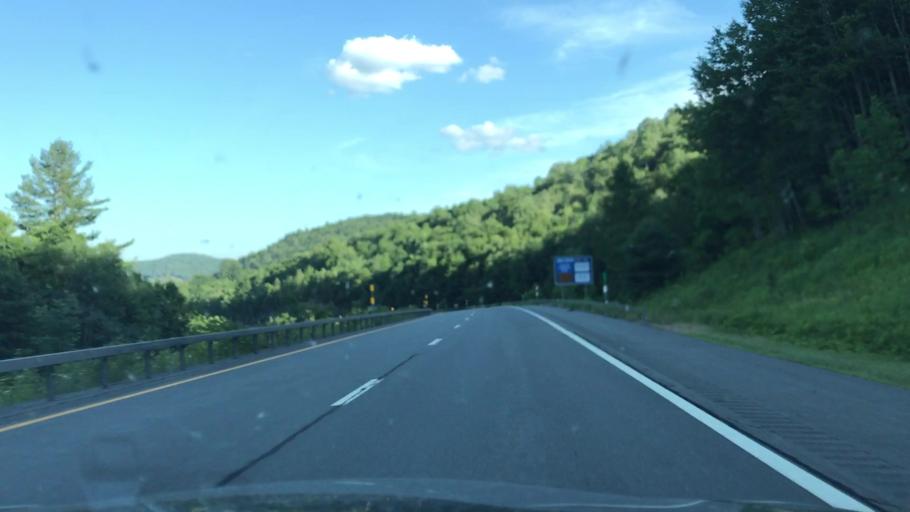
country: US
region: New York
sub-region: Sullivan County
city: Livingston Manor
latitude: 41.9399
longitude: -74.9289
